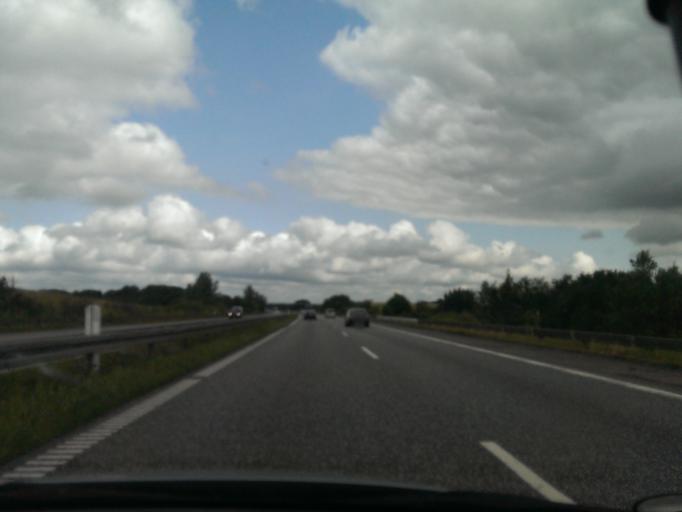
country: DK
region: North Denmark
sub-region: Mariagerfjord Kommune
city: Hobro
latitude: 56.6490
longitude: 9.7381
